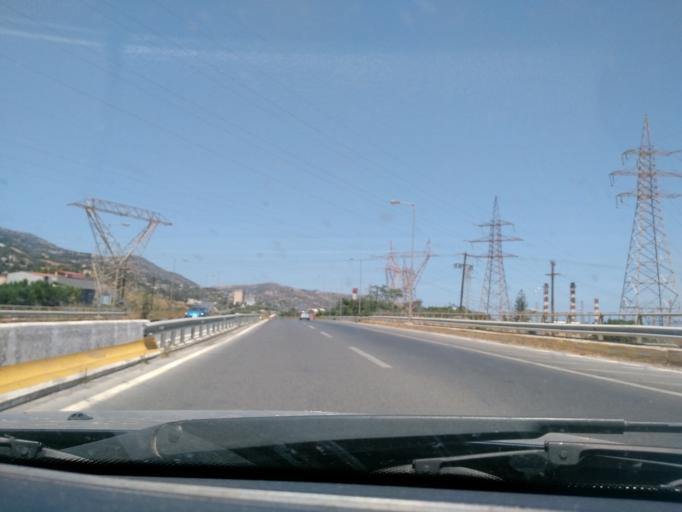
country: GR
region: Crete
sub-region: Nomos Irakleiou
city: Gazi
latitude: 35.3383
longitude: 25.0504
